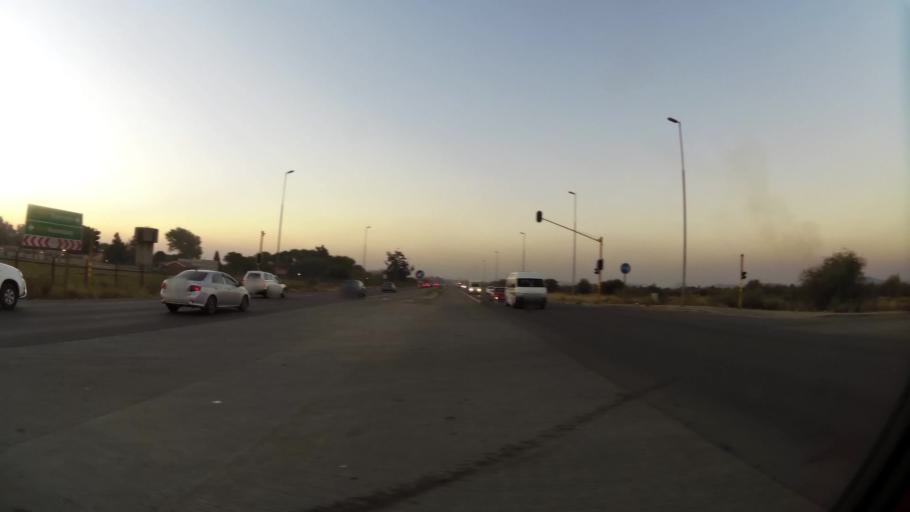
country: ZA
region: North-West
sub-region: Bojanala Platinum District Municipality
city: Rustenburg
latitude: -25.6401
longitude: 27.2630
